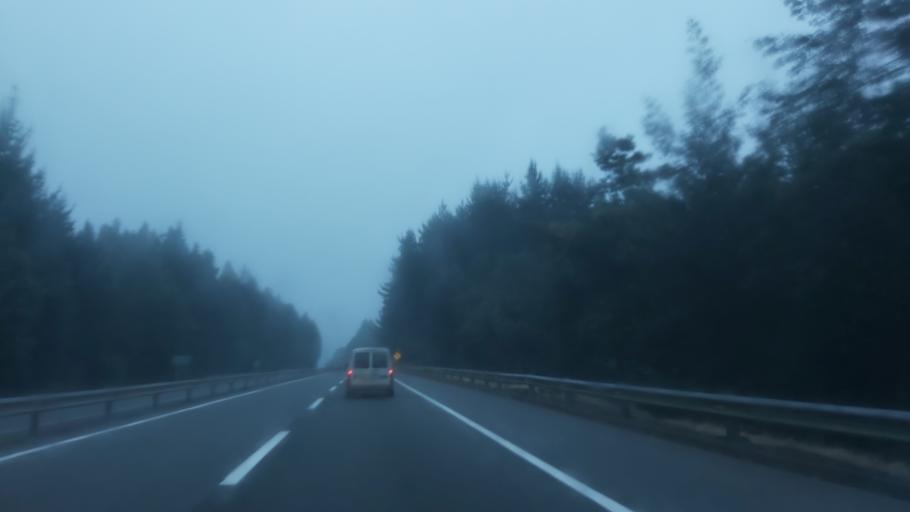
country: CL
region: Biobio
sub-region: Provincia de Concepcion
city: Penco
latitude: -36.7420
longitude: -72.9057
